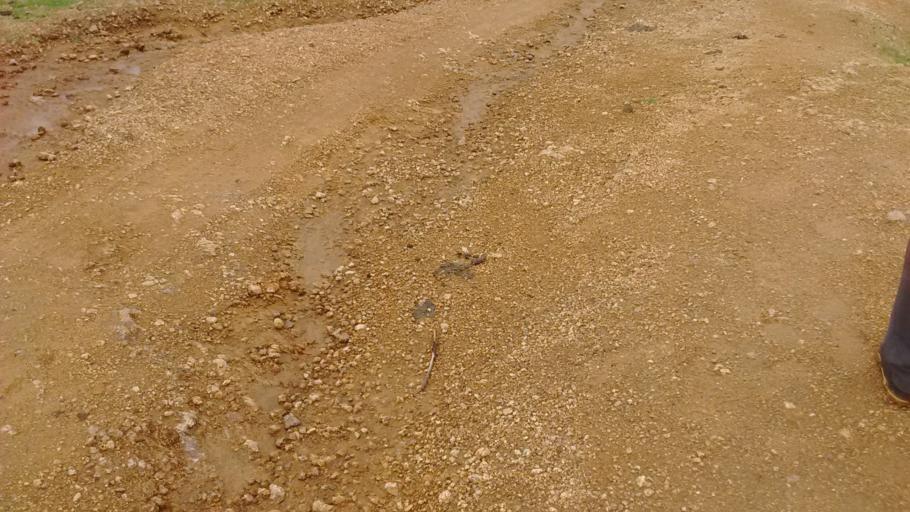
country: IN
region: Tamil Nadu
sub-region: Kancheepuram
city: Madambakkam
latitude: 12.9201
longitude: 80.0060
